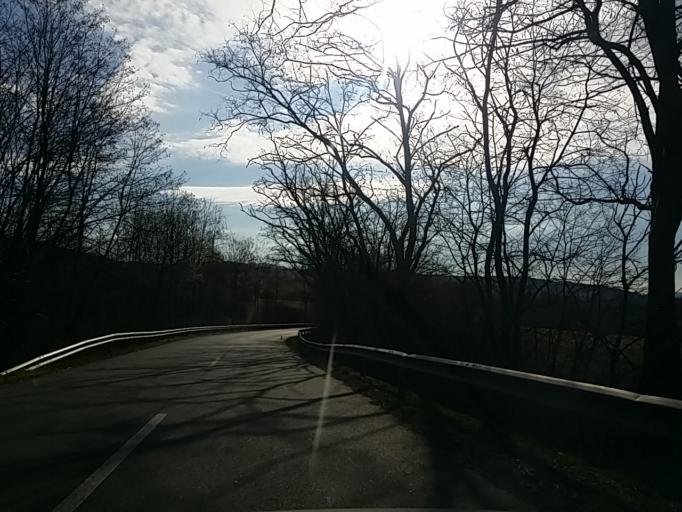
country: HU
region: Borsod-Abauj-Zemplen
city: Putnok
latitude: 48.4333
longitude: 20.4871
